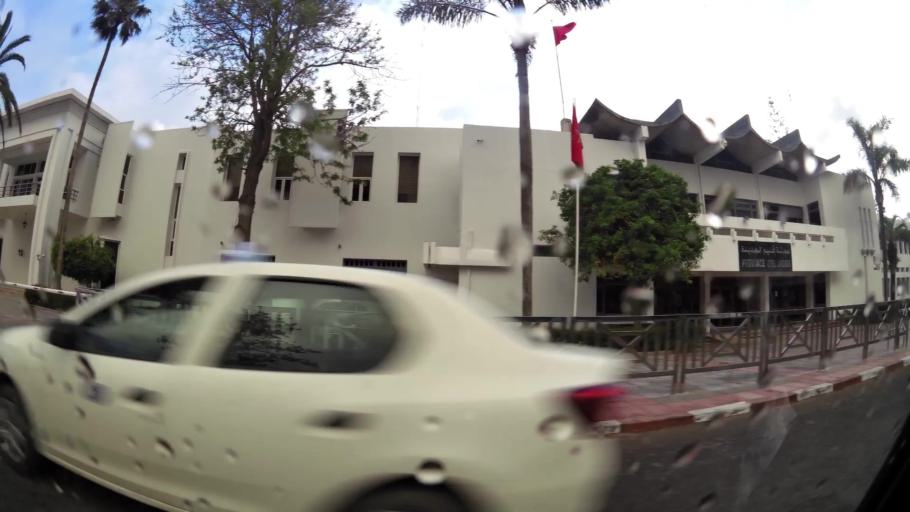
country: MA
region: Doukkala-Abda
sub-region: El-Jadida
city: El Jadida
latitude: 33.2449
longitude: -8.5057
